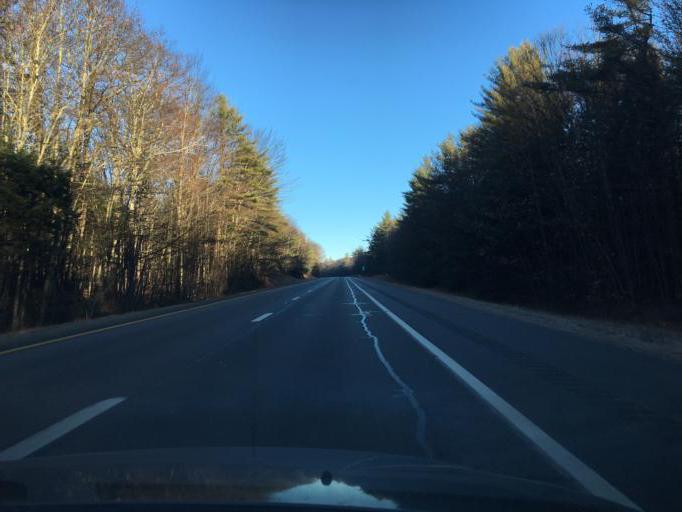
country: US
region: New Hampshire
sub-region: Belknap County
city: Sanbornton
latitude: 43.4869
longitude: -71.5936
